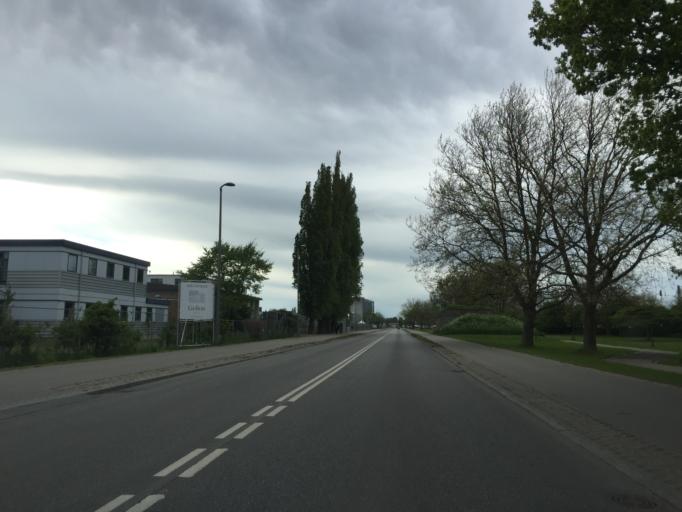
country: DK
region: Capital Region
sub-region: Kobenhavn
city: Christianshavn
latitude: 55.6656
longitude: 12.6288
